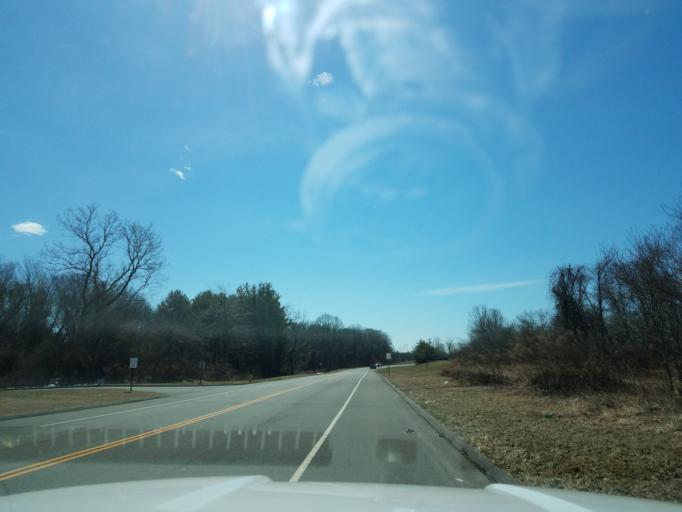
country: US
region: Connecticut
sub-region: New Haven County
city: Woodmont
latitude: 41.2605
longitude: -72.9968
